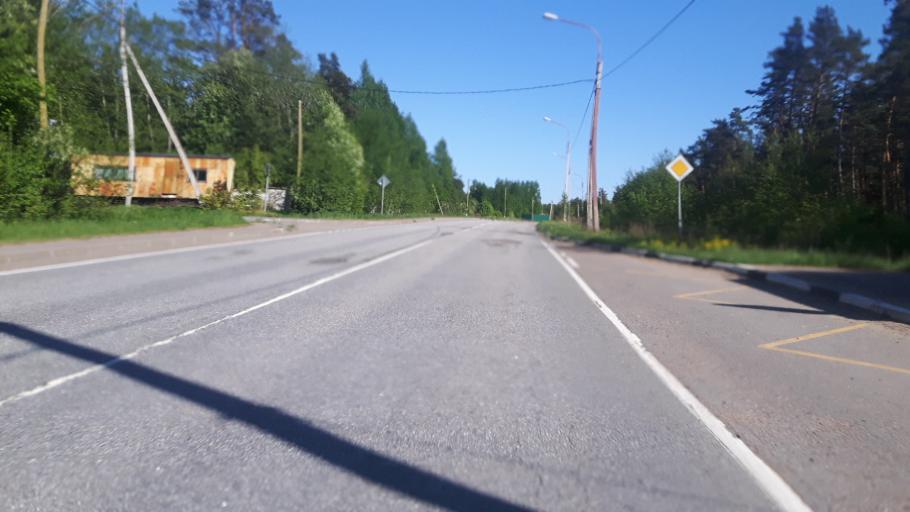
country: RU
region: Leningrad
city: Sosnovyy Bor
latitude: 60.1915
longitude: 29.0124
